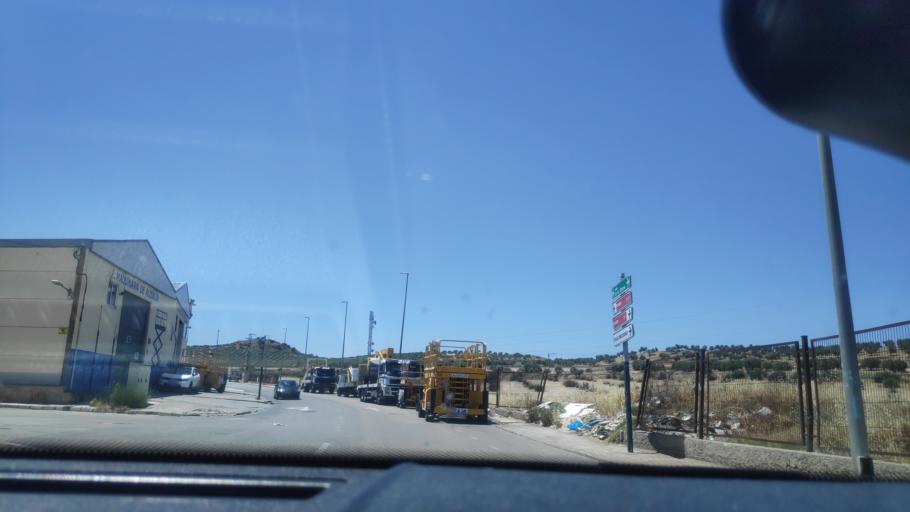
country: ES
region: Andalusia
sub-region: Provincia de Jaen
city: Jaen
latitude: 37.8042
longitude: -3.7820
